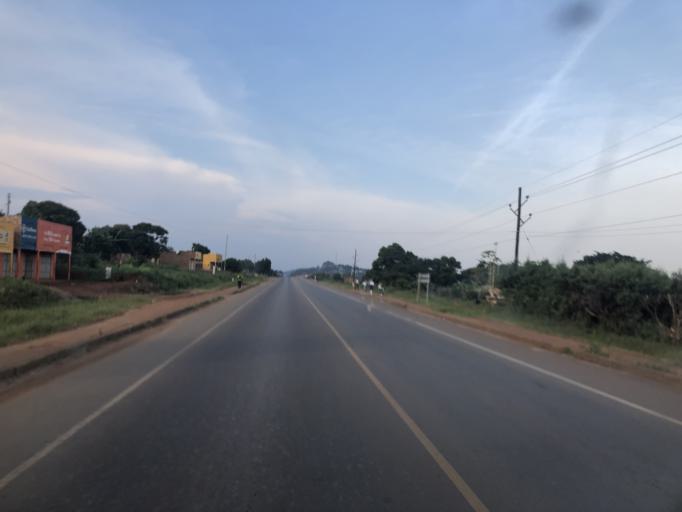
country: UG
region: Central Region
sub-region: Mpigi District
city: Mpigi
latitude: 0.2083
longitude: 32.3169
